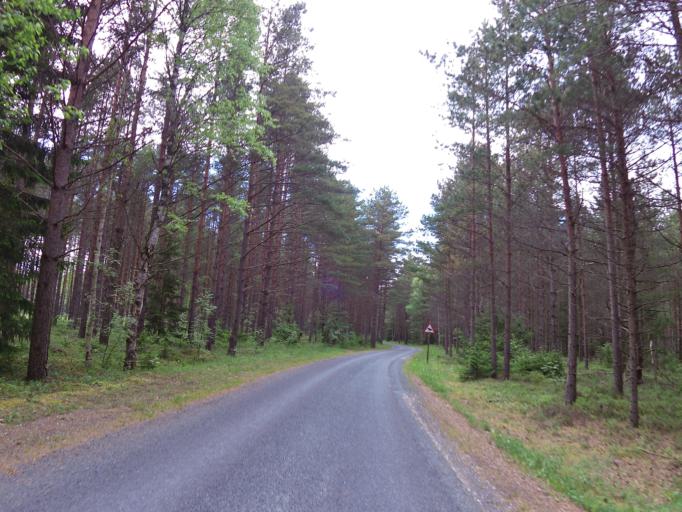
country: EE
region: Harju
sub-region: Paldiski linn
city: Paldiski
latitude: 59.2507
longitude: 23.7652
